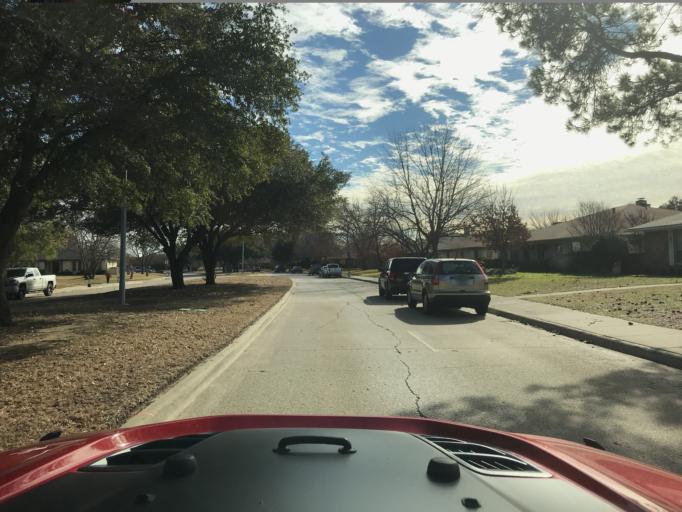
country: US
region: Texas
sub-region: Denton County
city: Lewisville
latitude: 33.0481
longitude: -97.0293
